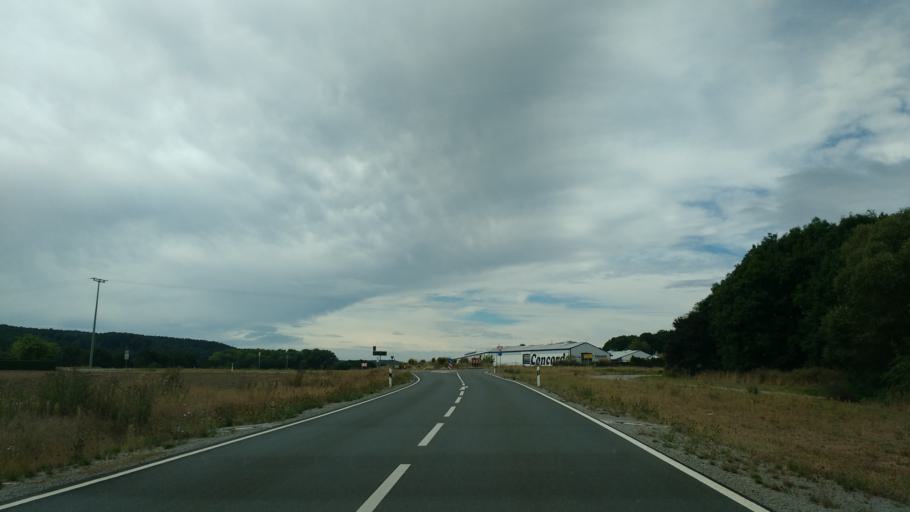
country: DE
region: Bavaria
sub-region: Regierungsbezirk Mittelfranken
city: Burghaslach
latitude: 49.7659
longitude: 10.5698
